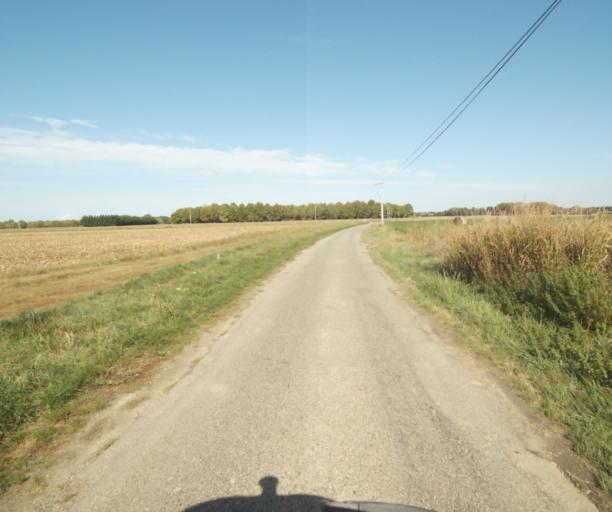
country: FR
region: Midi-Pyrenees
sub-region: Departement du Tarn-et-Garonne
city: Verdun-sur-Garonne
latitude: 43.8772
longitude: 1.2350
